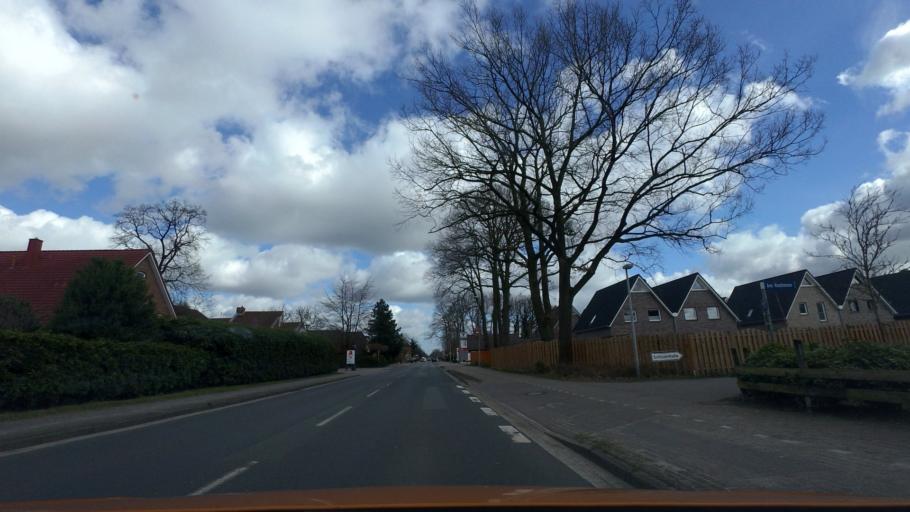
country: DE
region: Lower Saxony
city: Oldenburg
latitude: 53.1392
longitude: 8.1110
